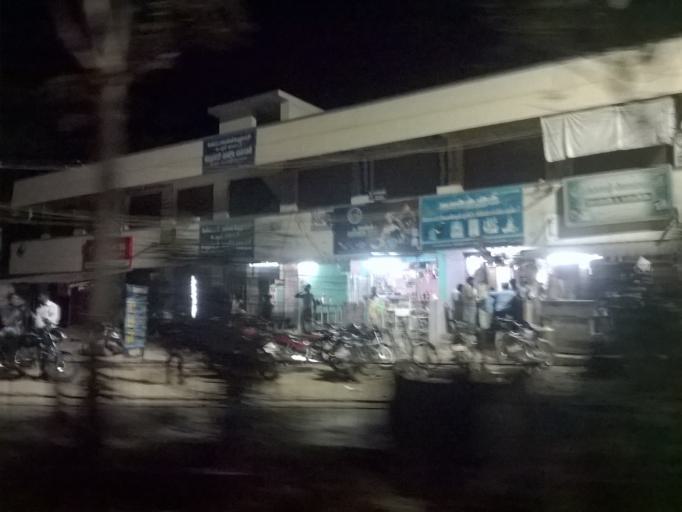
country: IN
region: Tamil Nadu
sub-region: Cuddalore
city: Nellikkuppam
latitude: 11.7868
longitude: 79.6313
